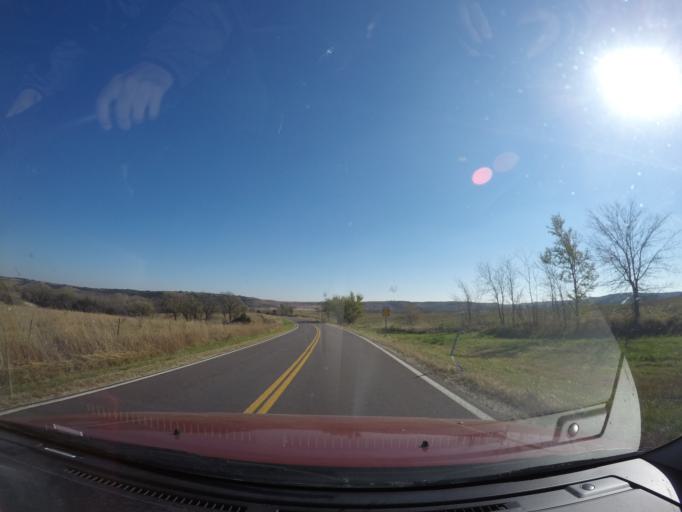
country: US
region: Kansas
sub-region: Geary County
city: Grandview Plaza
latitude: 39.0082
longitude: -96.7474
